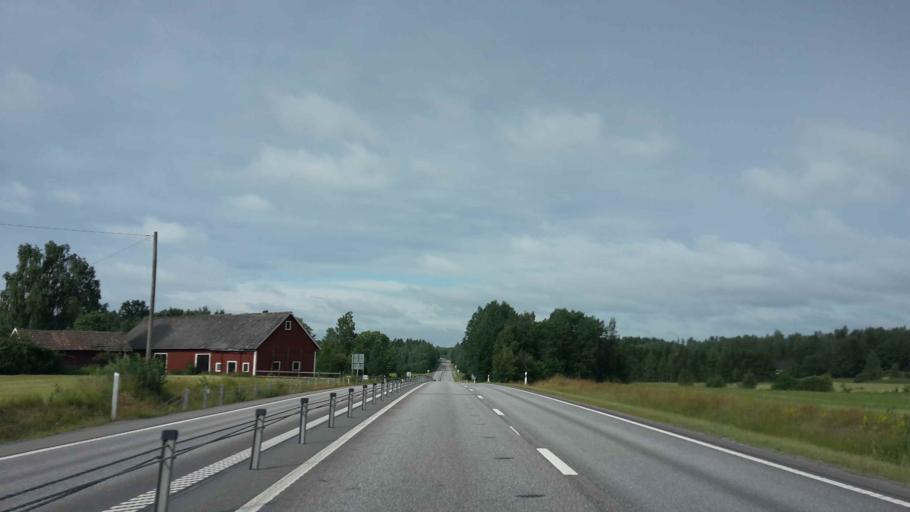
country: SE
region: OEstergoetland
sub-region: Motala Kommun
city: Motala
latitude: 58.5765
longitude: 15.0923
